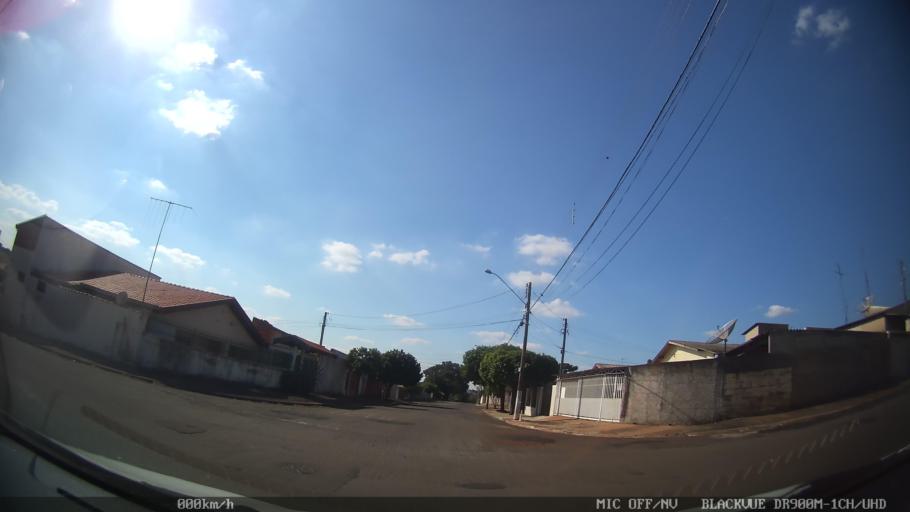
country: BR
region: Sao Paulo
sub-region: Sumare
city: Sumare
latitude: -22.8134
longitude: -47.2906
